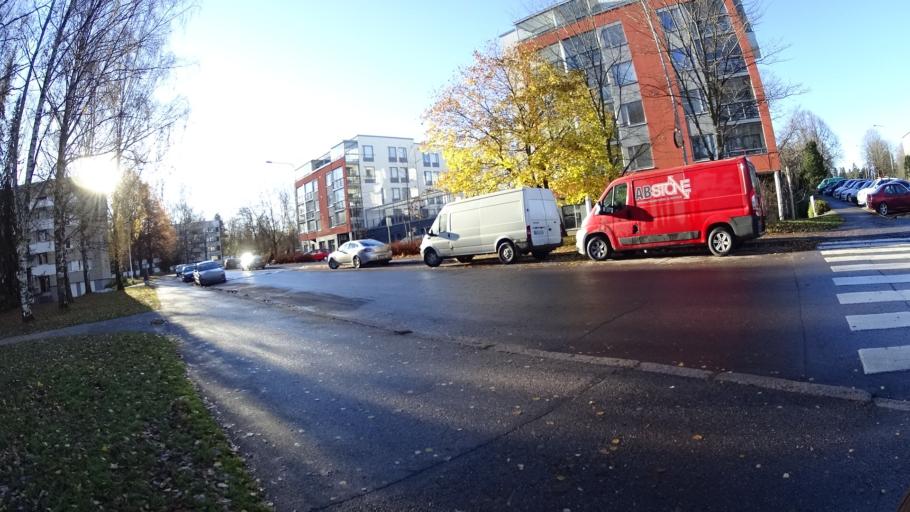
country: FI
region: Uusimaa
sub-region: Helsinki
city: Teekkarikylae
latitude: 60.2352
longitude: 24.8538
